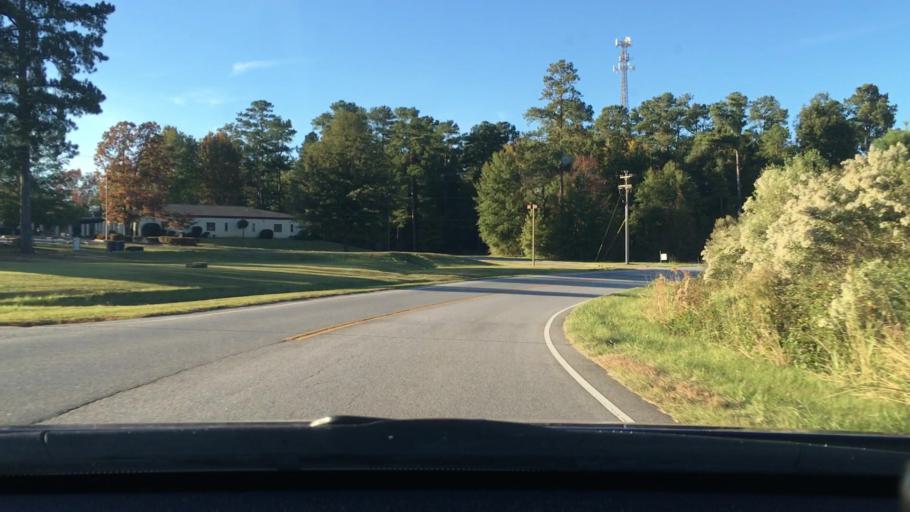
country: US
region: South Carolina
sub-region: Lexington County
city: Irmo
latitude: 34.0924
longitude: -81.1628
